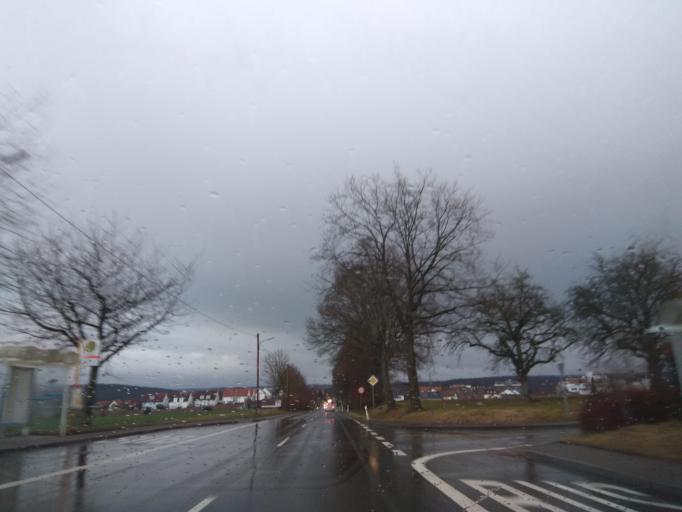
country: DE
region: Baden-Wuerttemberg
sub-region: Regierungsbezirk Stuttgart
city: Steinenbronn
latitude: 48.6999
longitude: 9.1175
